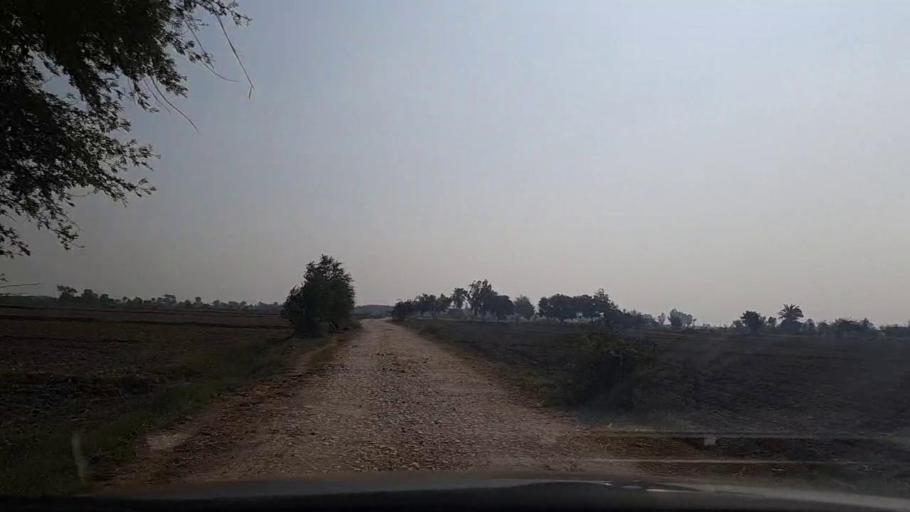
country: PK
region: Sindh
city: Mirpur Sakro
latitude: 24.5674
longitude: 67.7768
